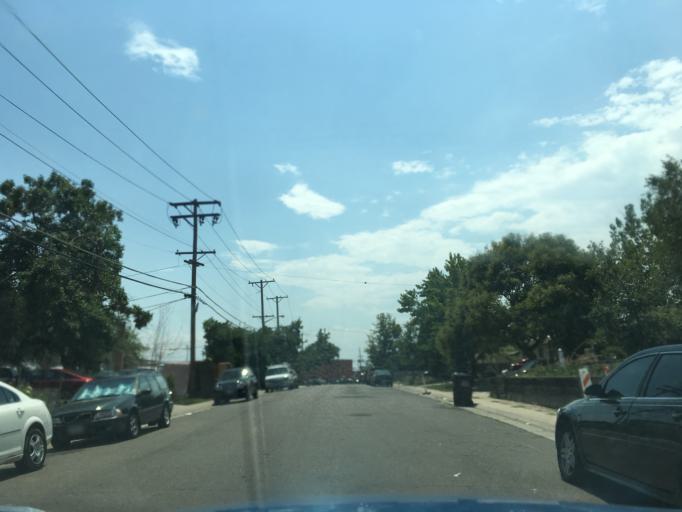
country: US
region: Colorado
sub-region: Arapahoe County
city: Sheridan
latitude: 39.6837
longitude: -105.0263
